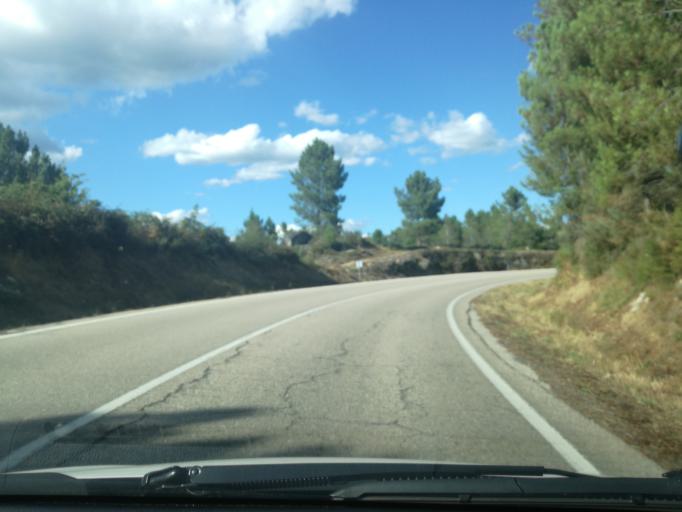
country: ES
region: Galicia
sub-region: Provincia de Ourense
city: Lobios
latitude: 41.8869
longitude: -8.0959
